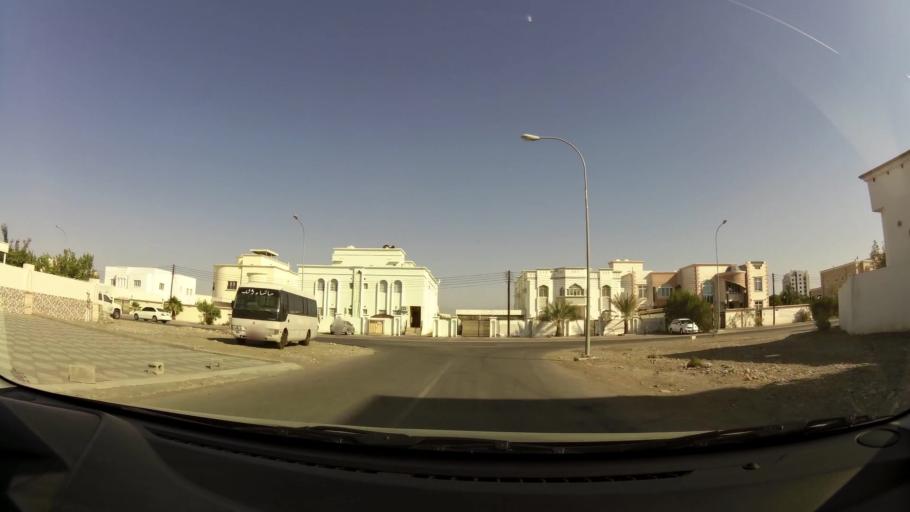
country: OM
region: Muhafazat Masqat
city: As Sib al Jadidah
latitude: 23.6183
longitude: 58.2074
